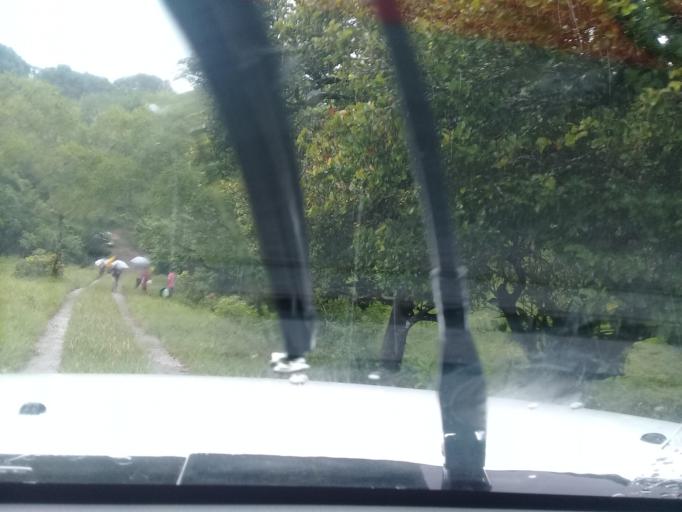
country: MX
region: Veracruz
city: Santiago Tuxtla
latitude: 18.4569
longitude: -95.3269
